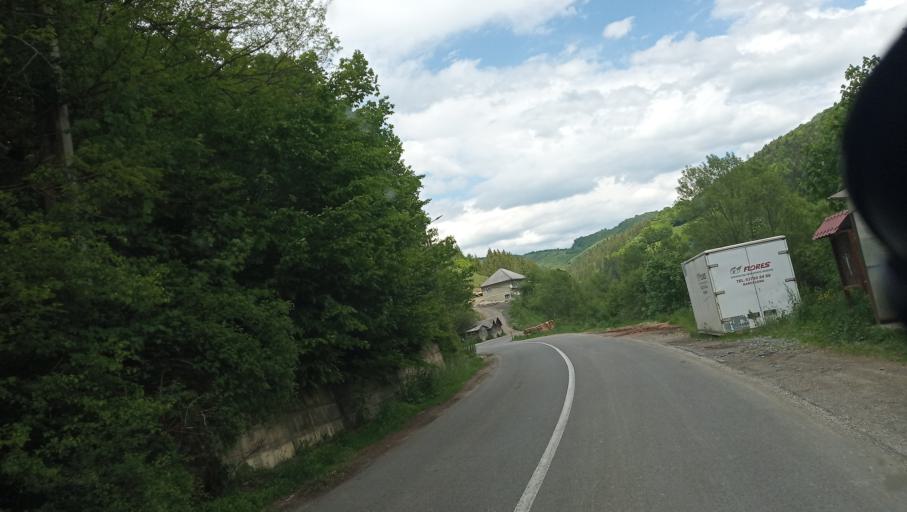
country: RO
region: Alba
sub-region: Comuna Ciuruleasa
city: Ciuruleasa
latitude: 46.2319
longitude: 23.0151
